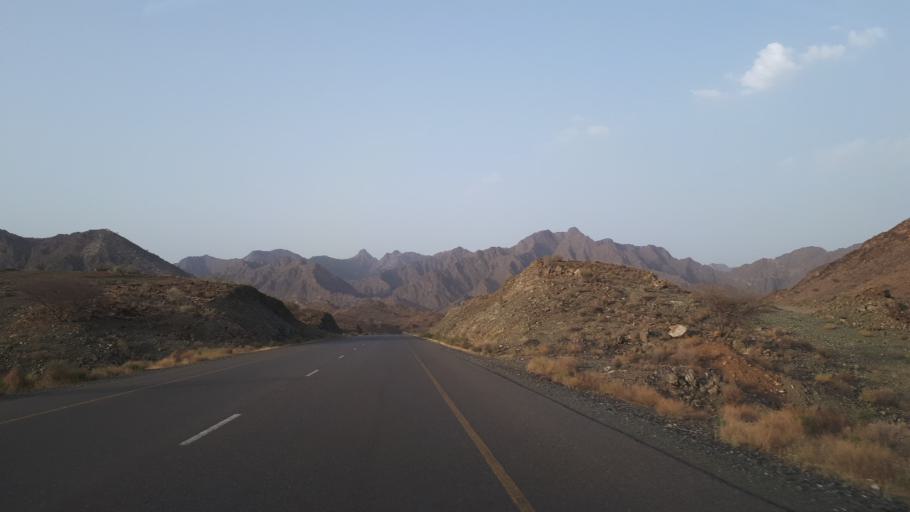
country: OM
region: Al Batinah
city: Rustaq
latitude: 23.4279
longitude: 57.1492
